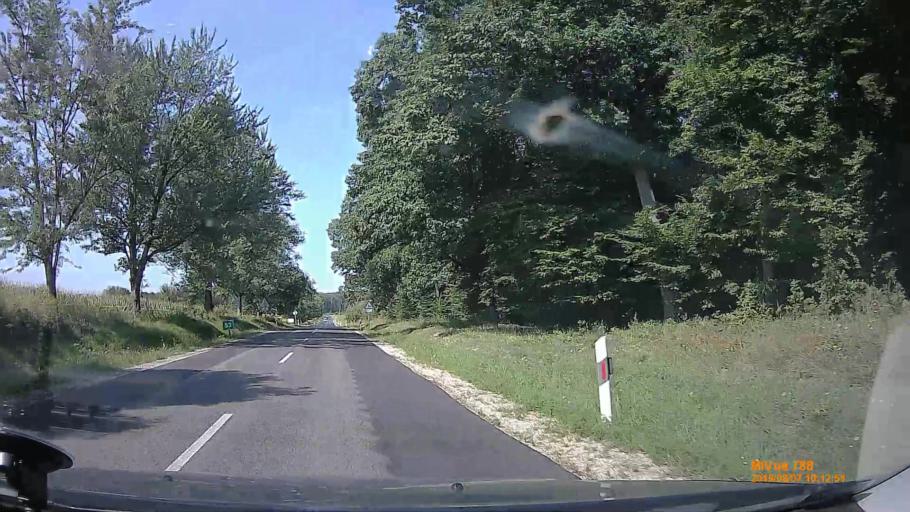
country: HU
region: Zala
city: Lenti
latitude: 46.6736
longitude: 16.6513
